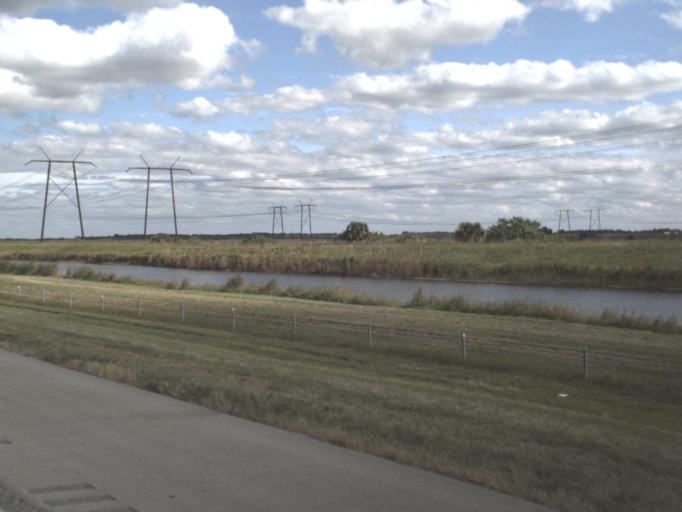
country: US
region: Florida
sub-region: Saint Lucie County
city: Lakewood Park
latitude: 27.4851
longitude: -80.5522
